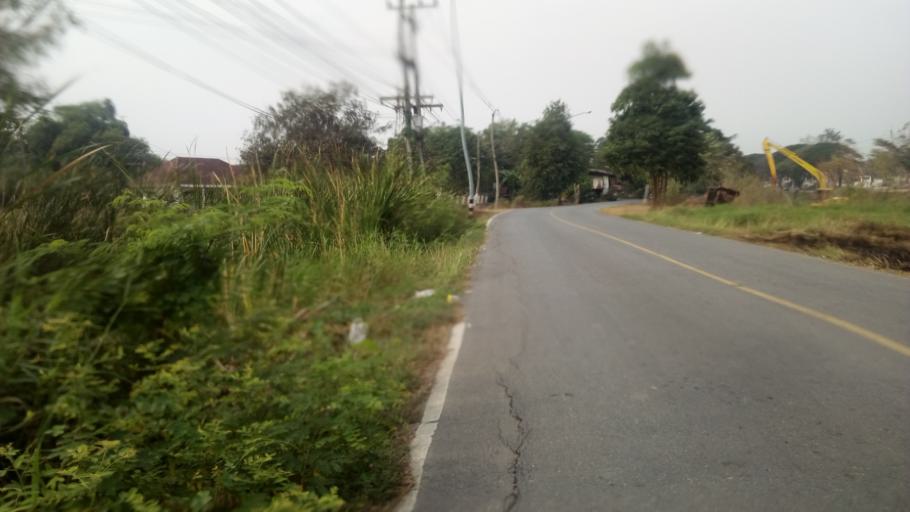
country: TH
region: Pathum Thani
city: Nong Suea
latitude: 14.0553
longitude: 100.8340
